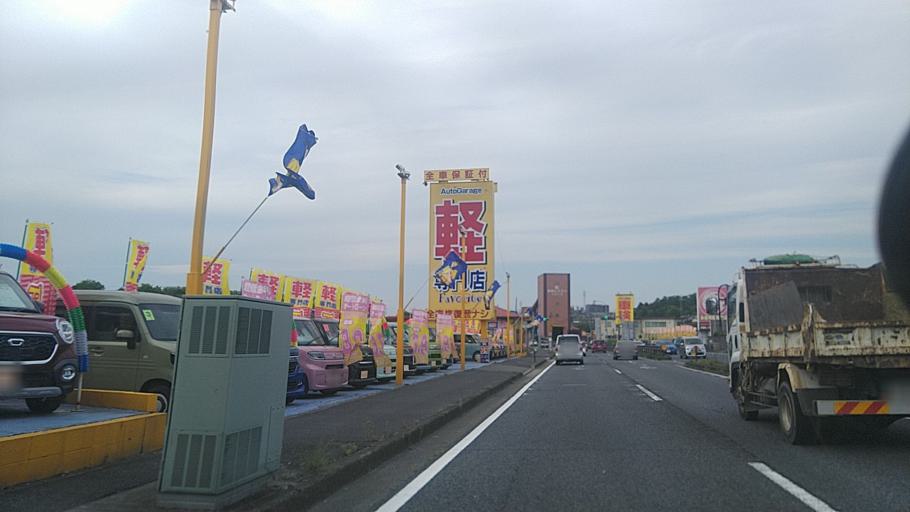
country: JP
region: Chiba
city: Yotsukaido
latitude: 35.7039
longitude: 140.1196
